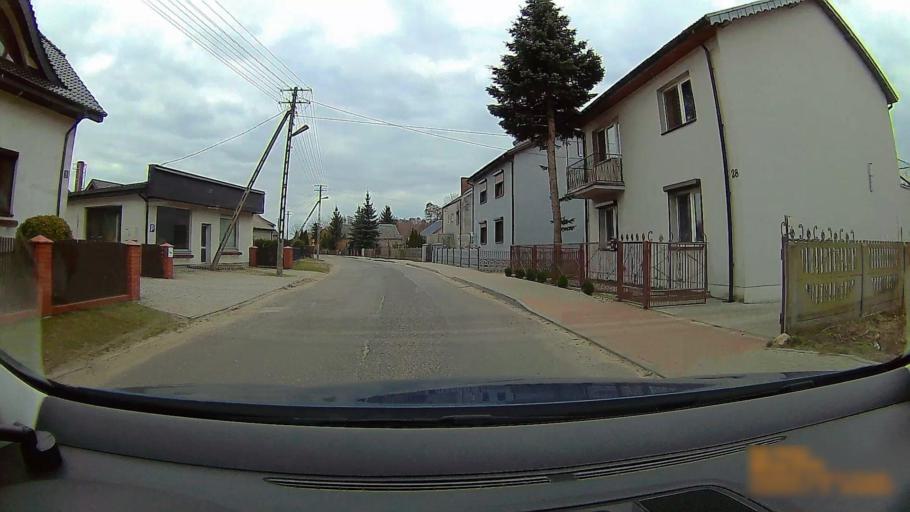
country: PL
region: Greater Poland Voivodeship
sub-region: Powiat koninski
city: Rzgow Pierwszy
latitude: 52.1299
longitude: 18.0613
